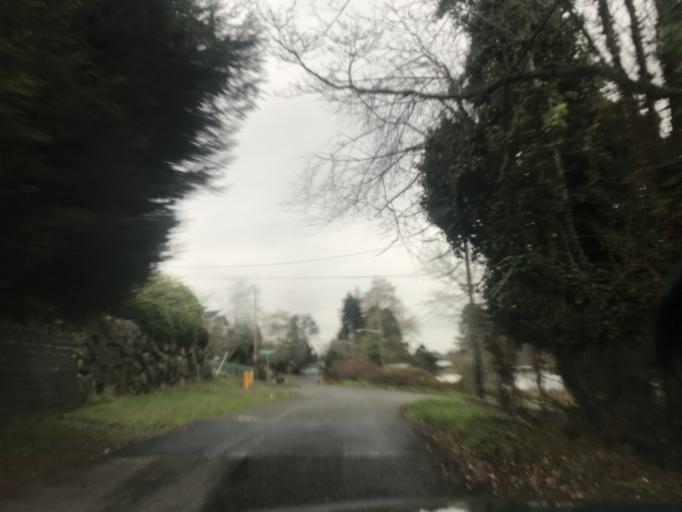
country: US
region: Washington
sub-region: King County
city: White Center
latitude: 47.5269
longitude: -122.3531
